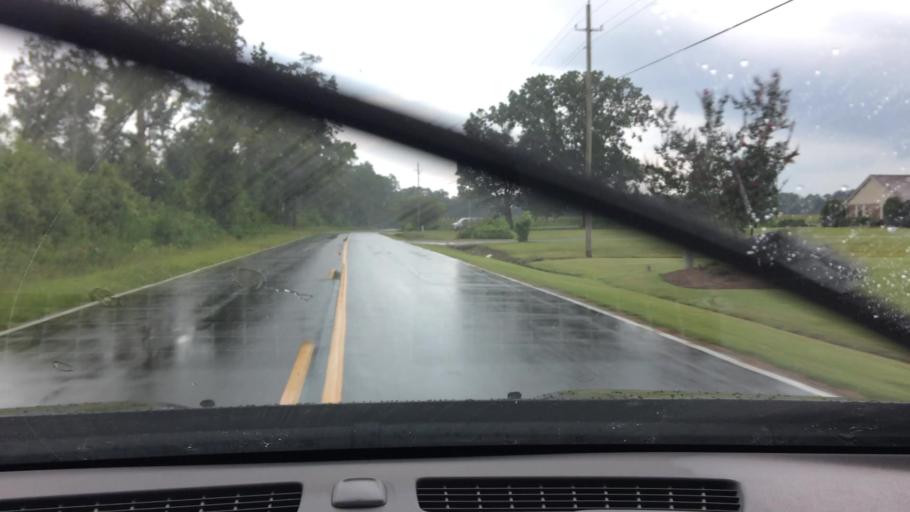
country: US
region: North Carolina
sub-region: Pitt County
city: Winterville
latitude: 35.5103
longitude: -77.3815
